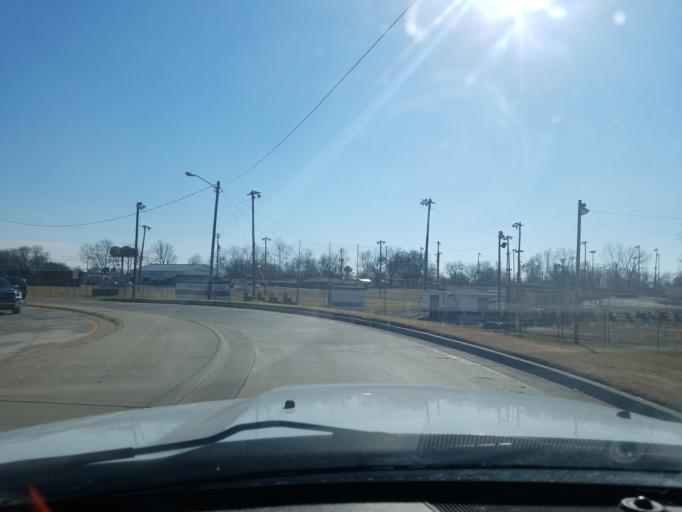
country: US
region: Kentucky
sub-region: Henderson County
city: Henderson
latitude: 37.8308
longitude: -87.5690
